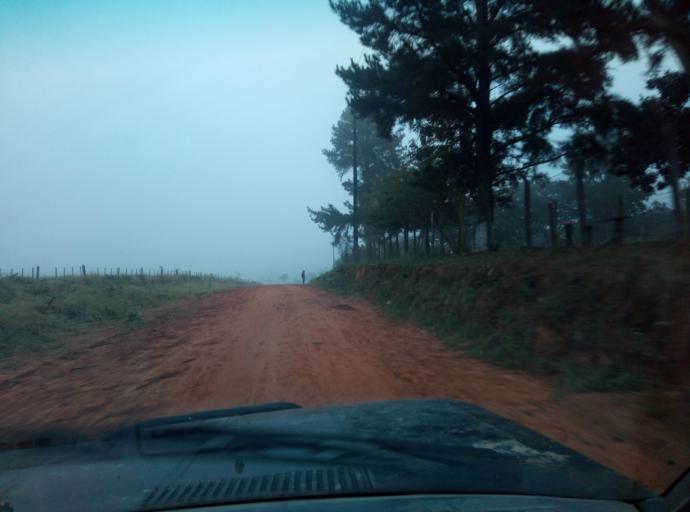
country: PY
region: Caaguazu
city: Doctor Cecilio Baez
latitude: -25.1578
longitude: -56.2515
